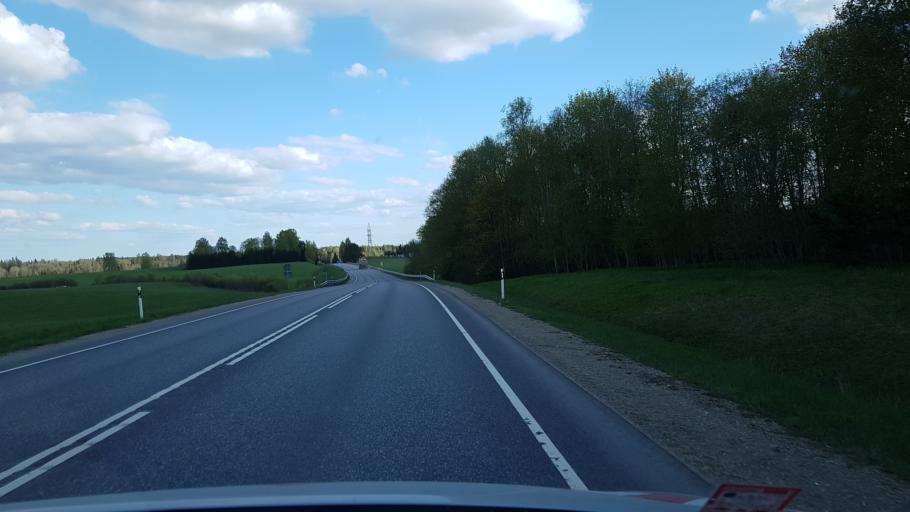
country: EE
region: Vorumaa
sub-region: Antsla vald
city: Vana-Antsla
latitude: 57.9863
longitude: 26.7682
